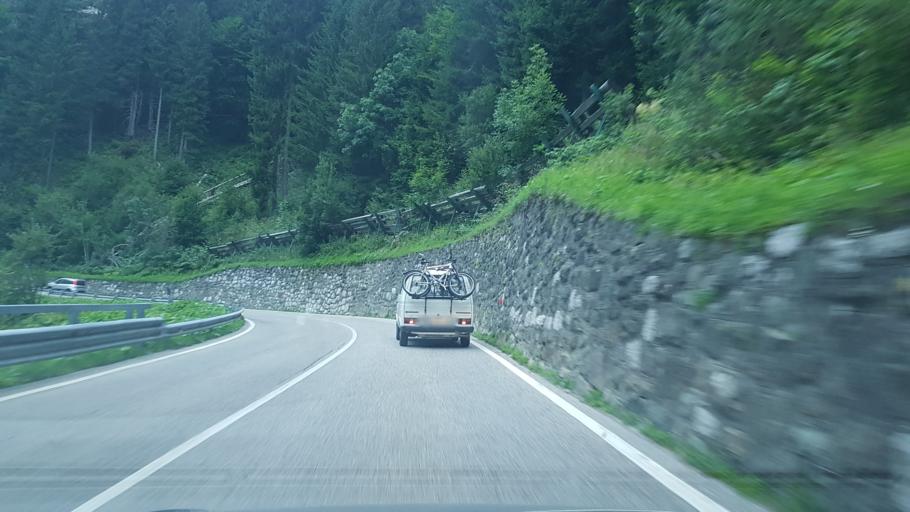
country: IT
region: Veneto
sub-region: Provincia di Belluno
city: Granvilla
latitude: 46.5671
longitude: 12.7269
